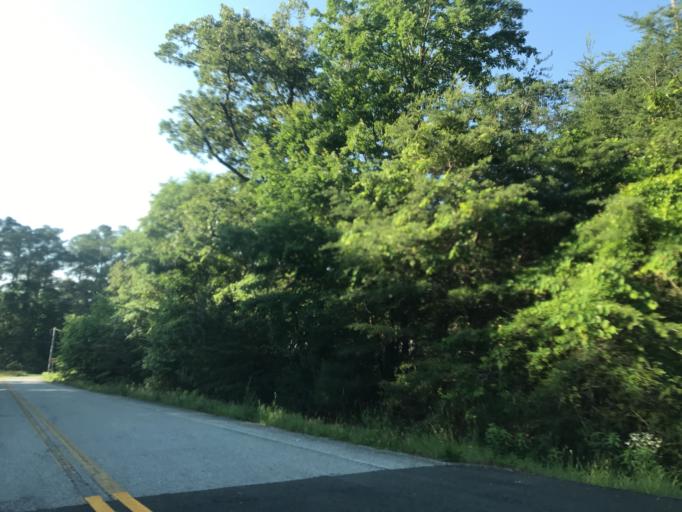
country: US
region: Maryland
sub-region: Wicomico County
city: Hebron
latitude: 38.5334
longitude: -75.7257
